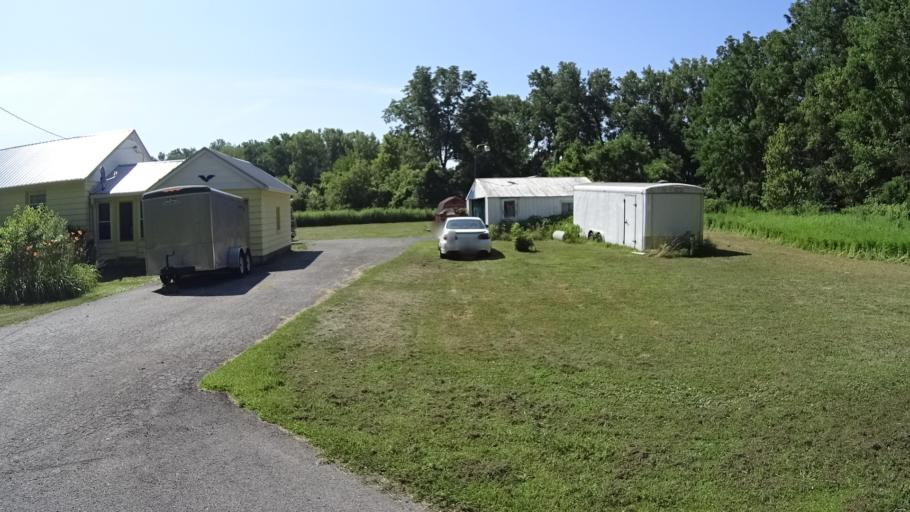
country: US
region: Ohio
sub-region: Huron County
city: Bellevue
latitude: 41.3912
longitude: -82.8366
